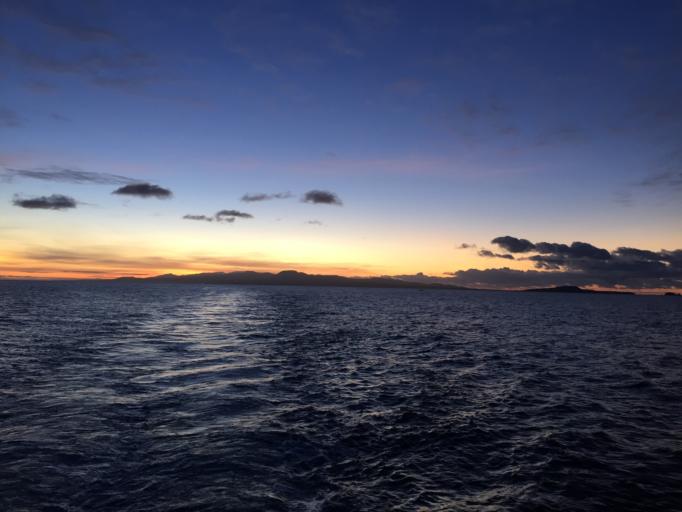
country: WS
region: Fa`asaleleaga
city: Safotulafai
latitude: -13.7732
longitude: -172.1669
